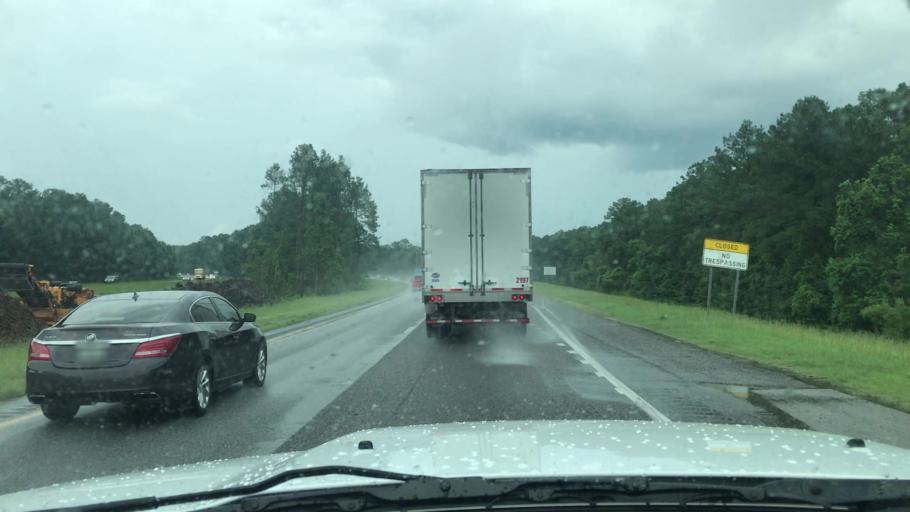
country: US
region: South Carolina
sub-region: Jasper County
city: Hardeeville
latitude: 32.2541
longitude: -81.1046
